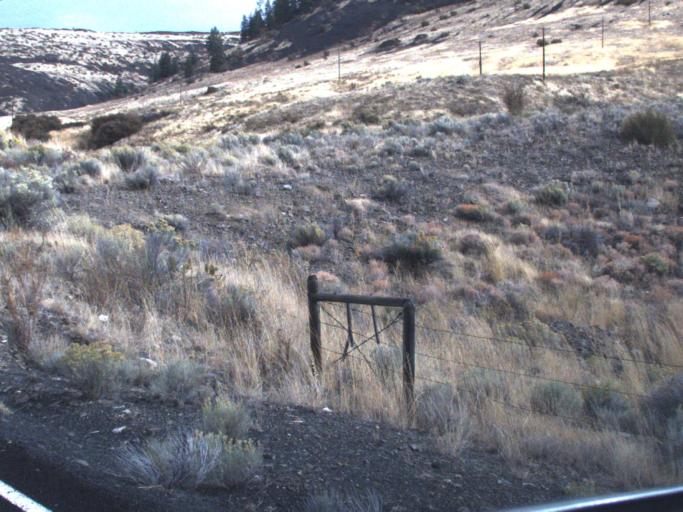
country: US
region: Washington
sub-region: Okanogan County
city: Coulee Dam
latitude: 47.9029
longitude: -118.6974
